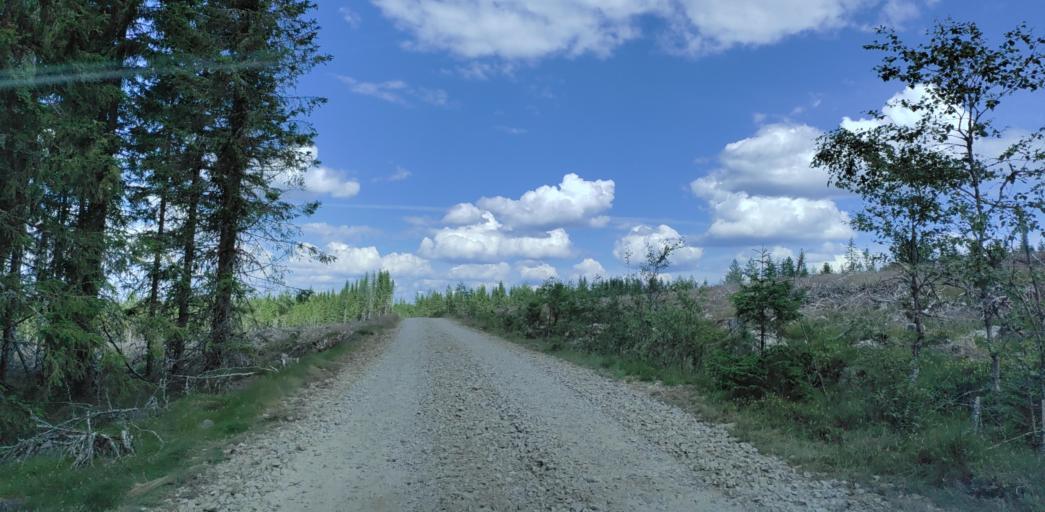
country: SE
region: Vaermland
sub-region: Hagfors Kommun
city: Ekshaerad
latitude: 60.0679
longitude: 13.3425
